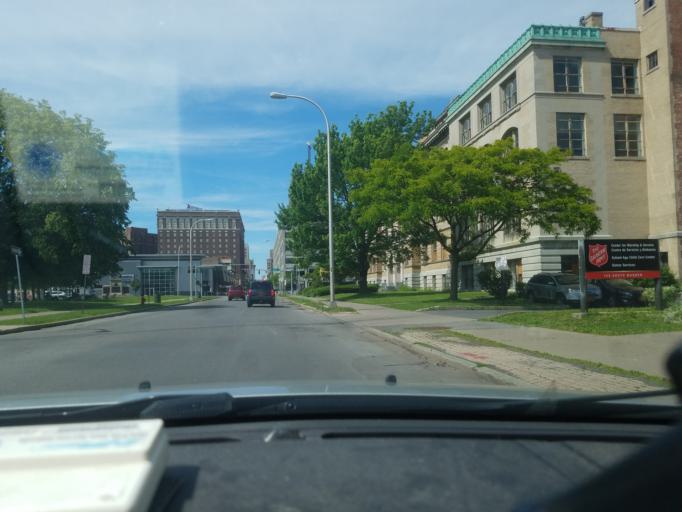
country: US
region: New York
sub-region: Onondaga County
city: Syracuse
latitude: 43.0417
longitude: -76.1509
